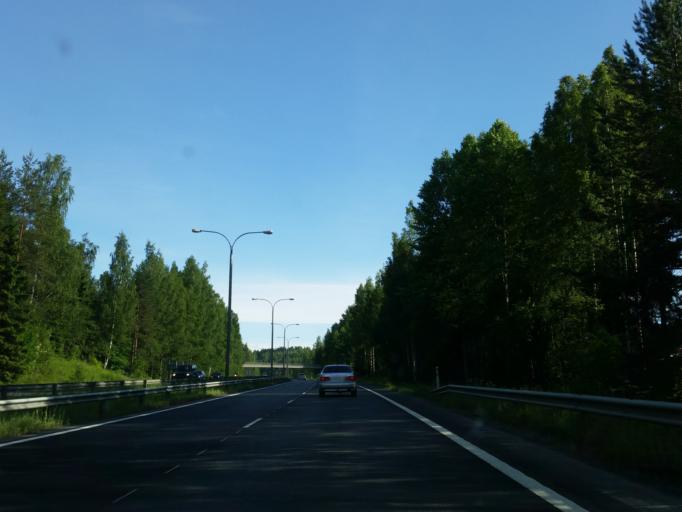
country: FI
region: Northern Savo
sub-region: Kuopio
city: Kuopio
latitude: 62.9235
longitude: 27.6756
